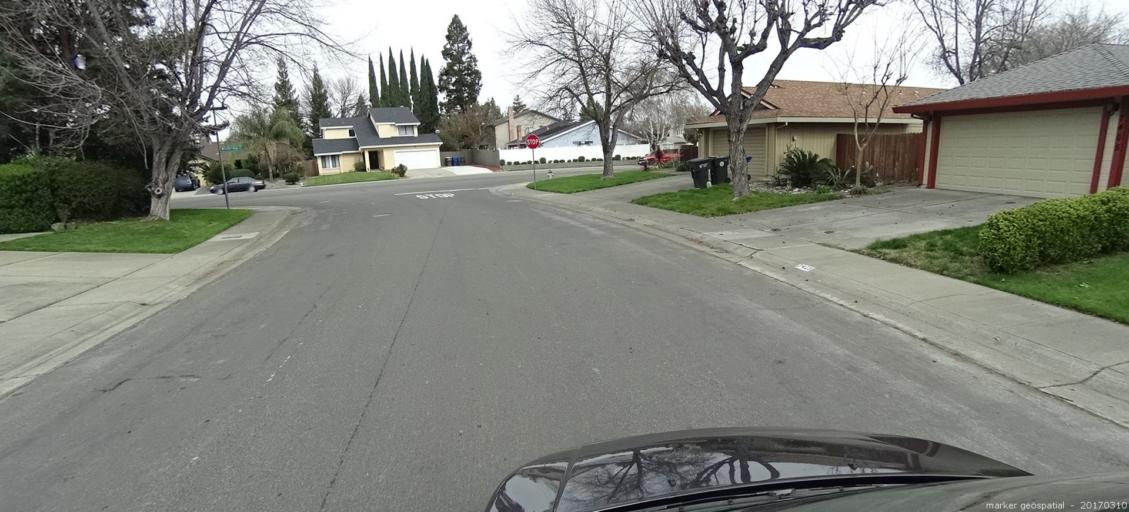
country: US
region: California
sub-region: Sacramento County
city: Parkway
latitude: 38.4883
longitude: -121.5277
